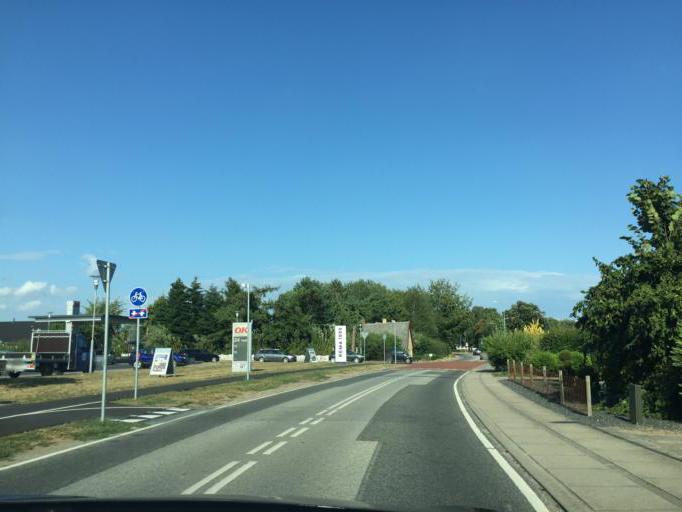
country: DK
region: South Denmark
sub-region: Faaborg-Midtfyn Kommune
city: Arslev
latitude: 55.3052
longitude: 10.4686
